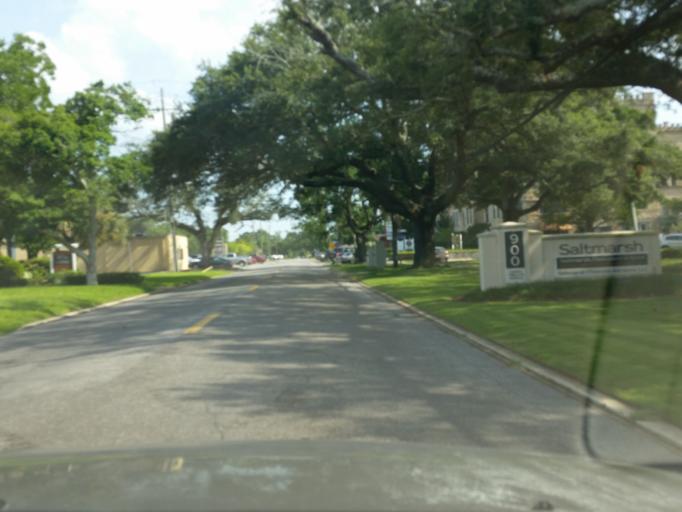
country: US
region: Florida
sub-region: Escambia County
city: Pensacola
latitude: 30.4251
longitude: -87.2029
